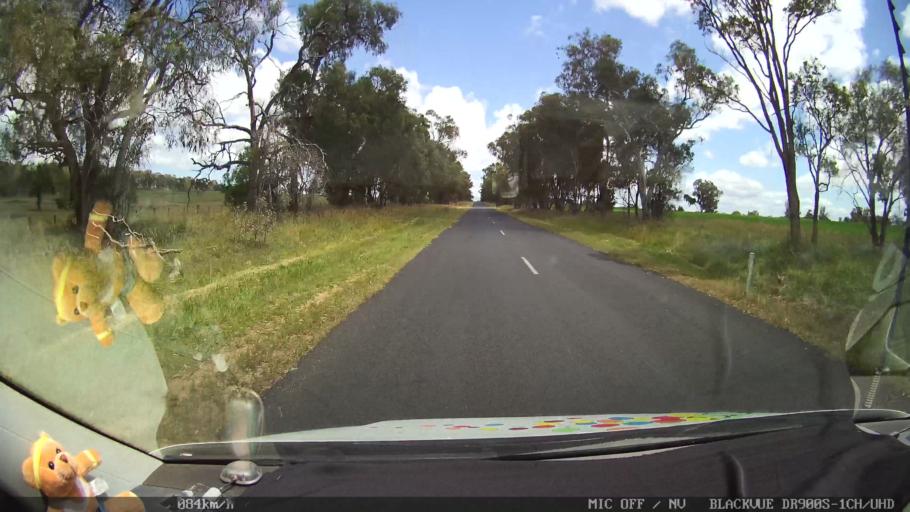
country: AU
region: New South Wales
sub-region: Glen Innes Severn
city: Glen Innes
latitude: -29.4820
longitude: 151.6837
